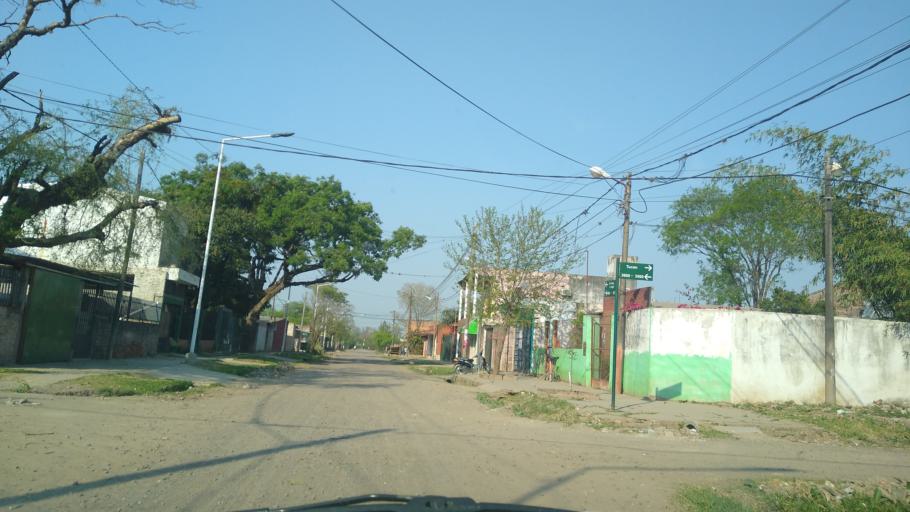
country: AR
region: Chaco
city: Barranqueras
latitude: -27.4744
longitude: -58.9483
